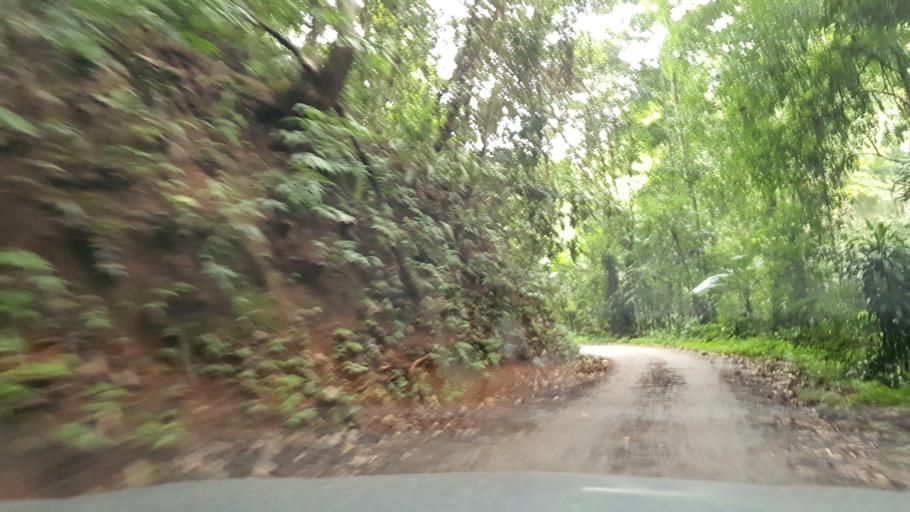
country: TH
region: Chiang Mai
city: Mae On
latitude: 18.9442
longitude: 99.3085
